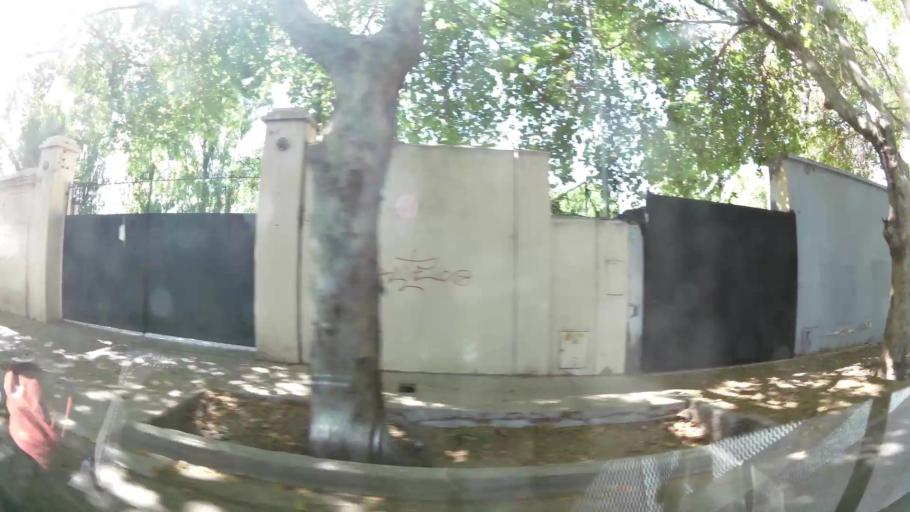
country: AR
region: Mendoza
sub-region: Departamento de Godoy Cruz
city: Godoy Cruz
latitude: -32.9599
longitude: -68.8627
